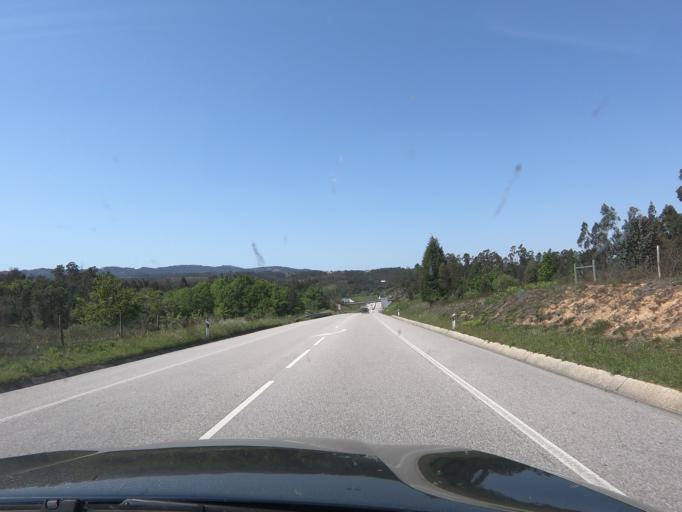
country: PT
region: Coimbra
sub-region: Vila Nova de Poiares
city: Poiares
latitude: 40.1692
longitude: -8.2663
